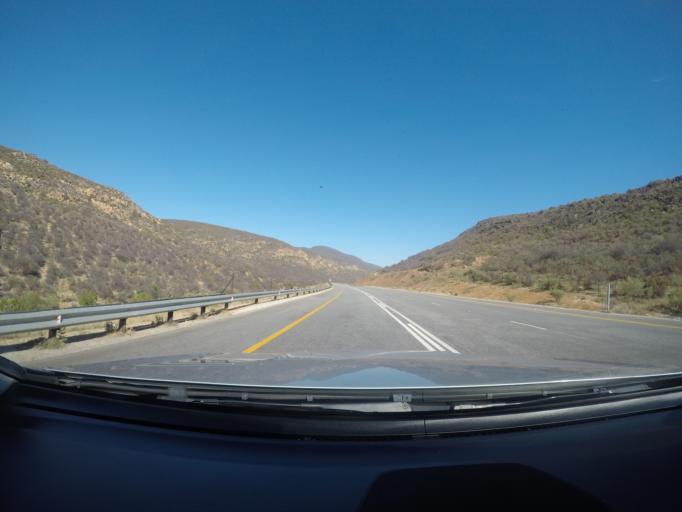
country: ZA
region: Western Cape
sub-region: West Coast District Municipality
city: Clanwilliam
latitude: -32.2612
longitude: 18.8671
